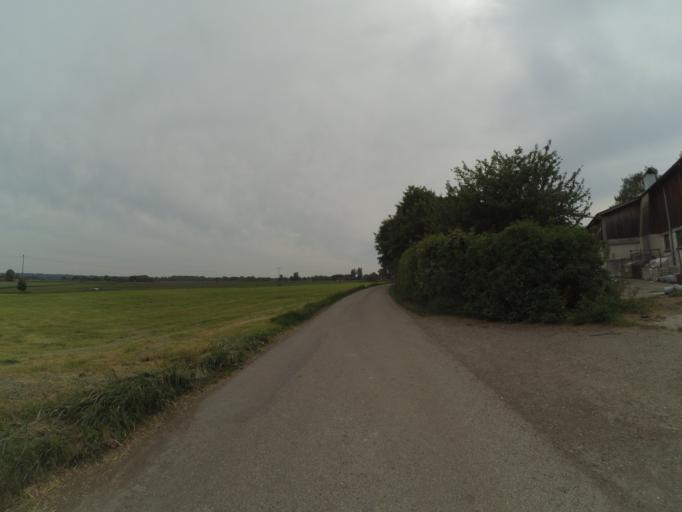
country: DE
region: Baden-Wuerttemberg
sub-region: Regierungsbezirk Stuttgart
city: Niederstotzingen
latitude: 48.5143
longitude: 10.2672
